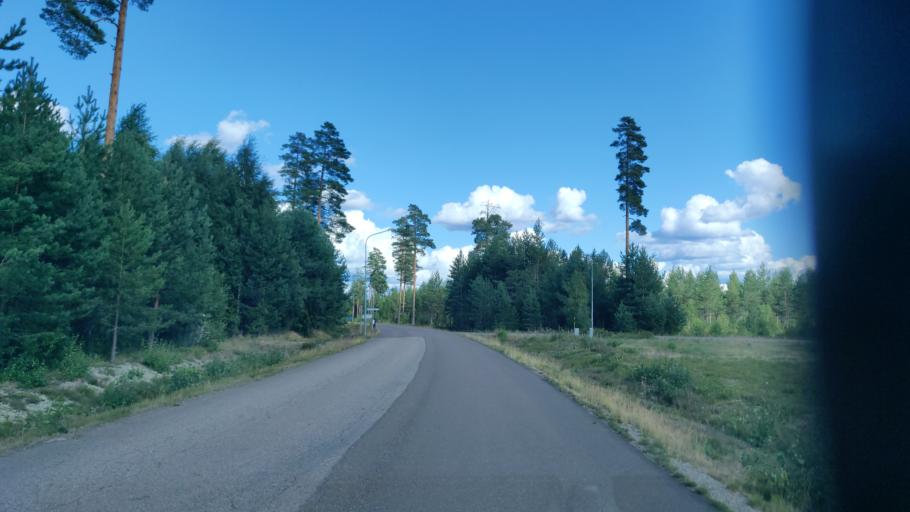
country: SE
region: Vaermland
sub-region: Hagfors Kommun
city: Hagfors
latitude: 60.0262
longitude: 13.5830
